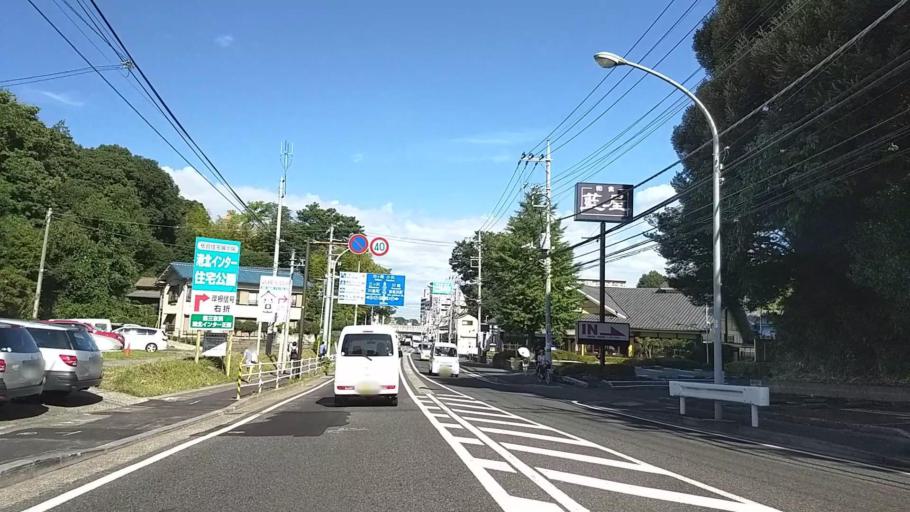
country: JP
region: Kanagawa
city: Yokohama
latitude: 35.4993
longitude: 139.6118
